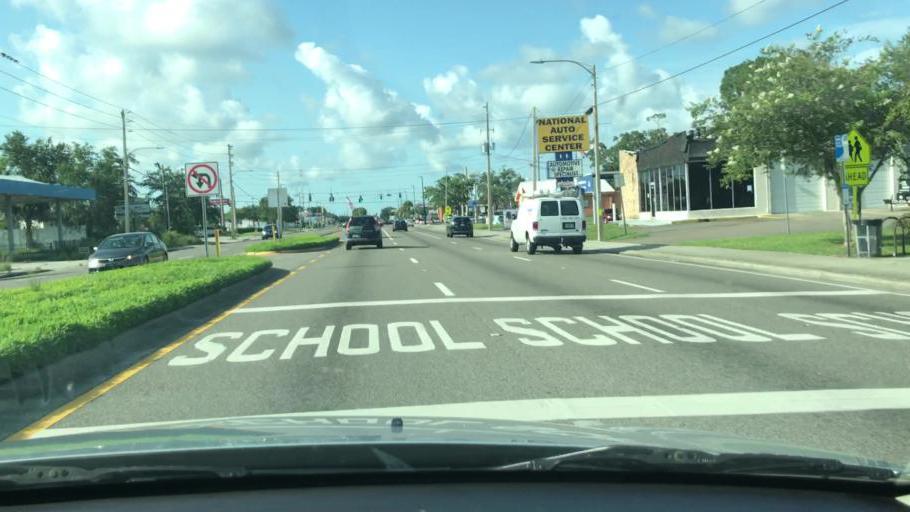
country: US
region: Florida
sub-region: Pinellas County
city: Pinellas Park
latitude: 27.8442
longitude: -82.7001
